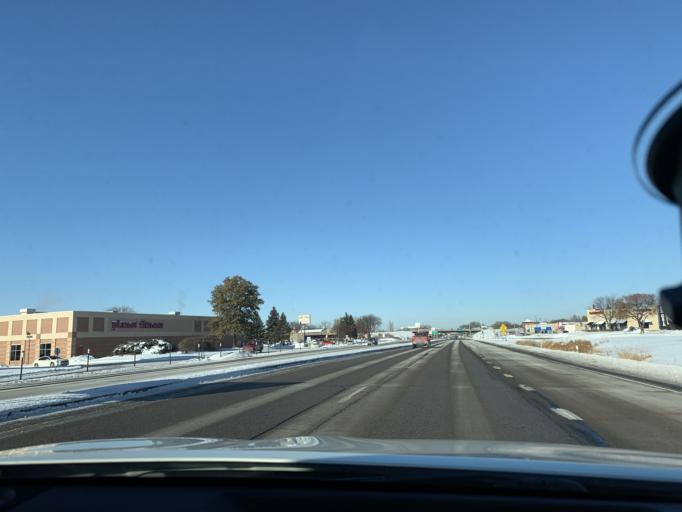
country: US
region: Minnesota
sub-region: Anoka County
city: Coon Rapids
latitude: 45.1329
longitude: -93.2663
